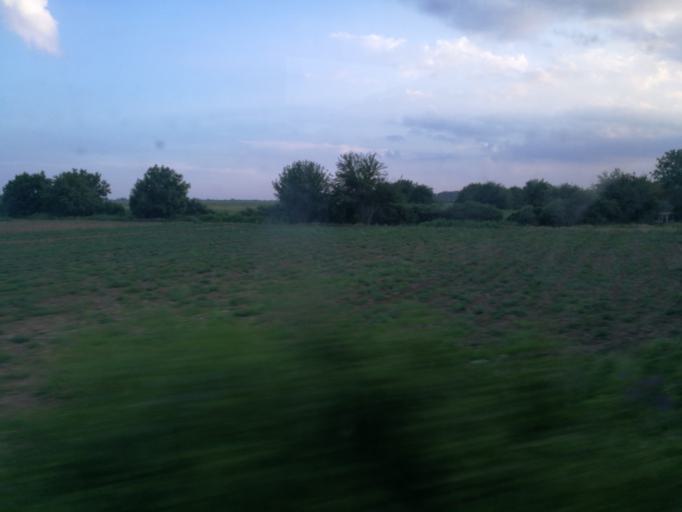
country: RO
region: Dambovita
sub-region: Comuna Contesti
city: Balteni
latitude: 44.6554
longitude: 25.6622
